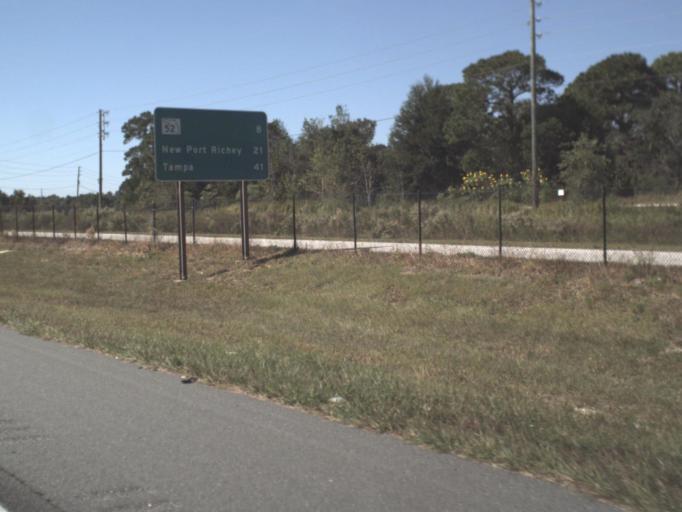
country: US
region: Florida
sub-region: Hernando County
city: Masaryktown
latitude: 28.4202
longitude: -82.4898
